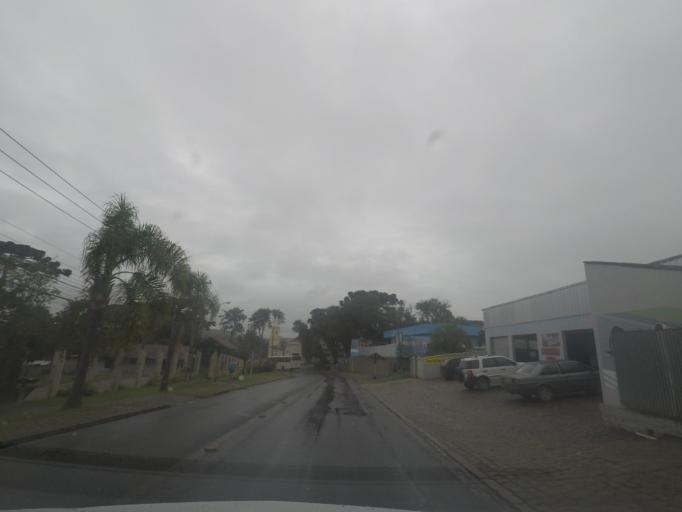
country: BR
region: Parana
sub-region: Quatro Barras
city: Quatro Barras
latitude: -25.3771
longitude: -49.1163
